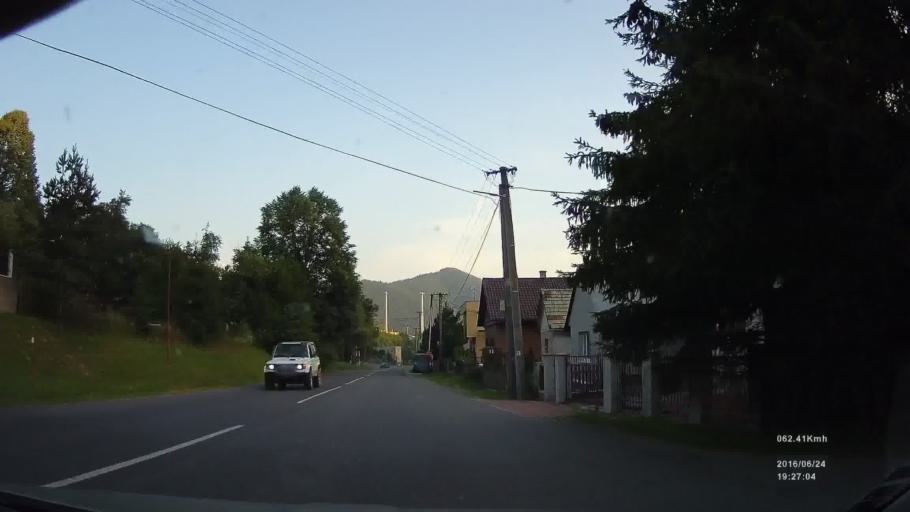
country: SK
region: Banskobystricky
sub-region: Okres Banska Bystrica
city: Brezno
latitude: 48.8193
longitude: 19.5611
